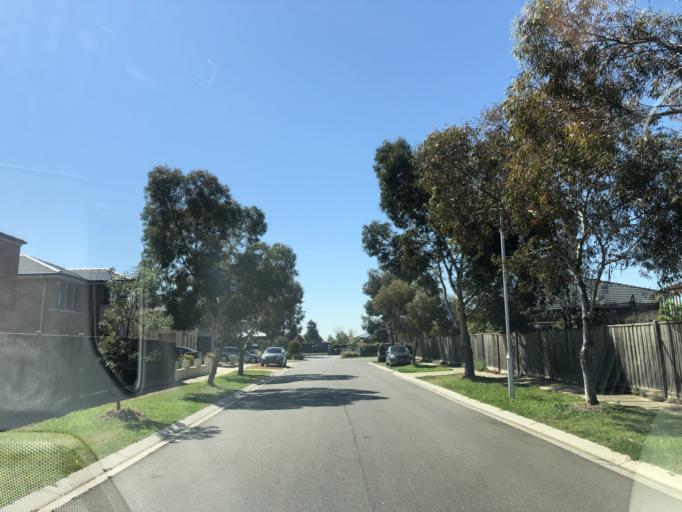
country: AU
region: Victoria
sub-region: Wyndham
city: Point Cook
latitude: -37.9077
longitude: 144.7242
